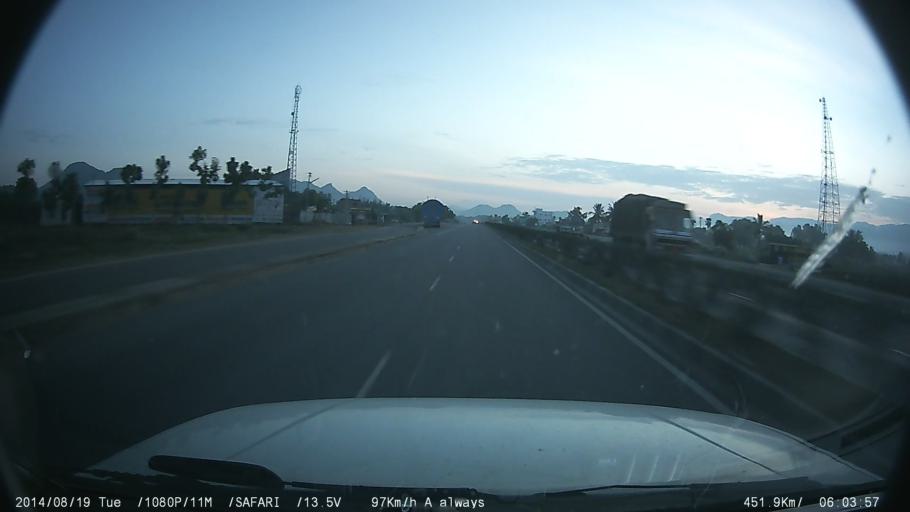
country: IN
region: Tamil Nadu
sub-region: Salem
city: Omalur
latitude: 11.8587
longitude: 78.0756
